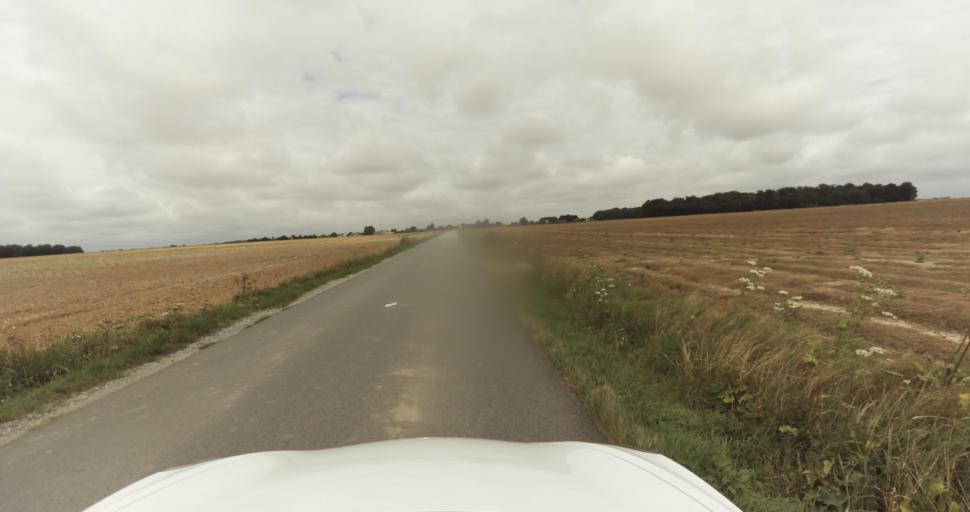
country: FR
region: Haute-Normandie
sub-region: Departement de l'Eure
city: Claville
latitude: 49.0366
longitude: 1.0269
